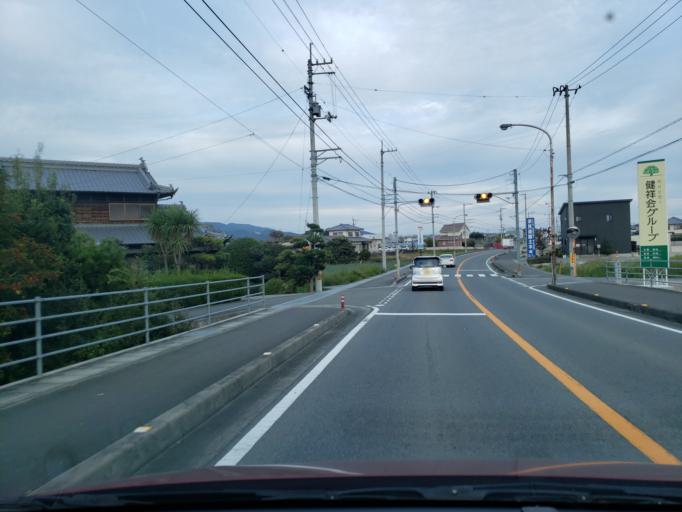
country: JP
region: Tokushima
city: Kamojimacho-jogejima
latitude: 34.0996
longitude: 134.3306
